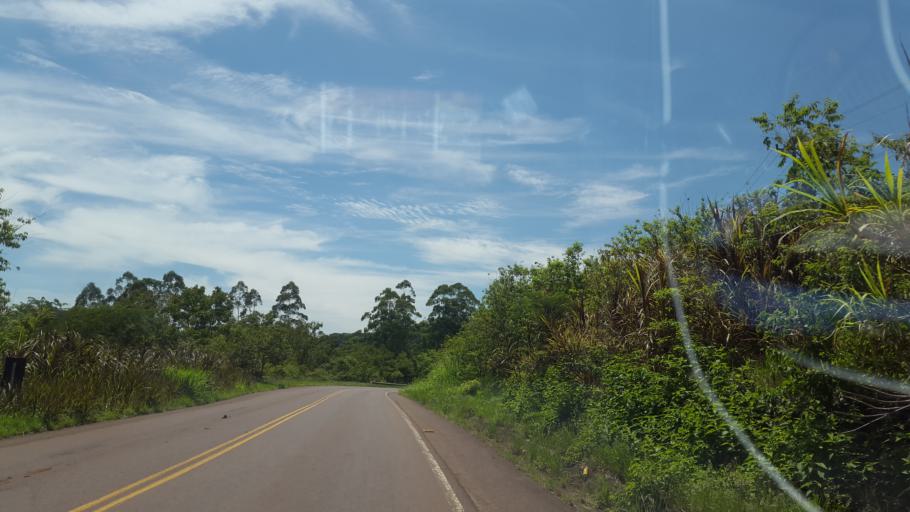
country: BR
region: Rio Grande do Sul
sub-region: Frederico Westphalen
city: Frederico Westphalen
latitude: -27.0744
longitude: -53.4193
